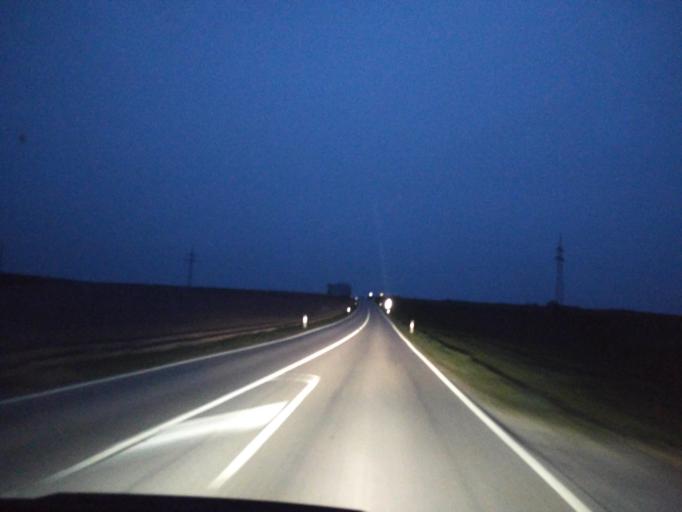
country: DE
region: Bavaria
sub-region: Upper Bavaria
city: Griesstatt
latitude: 47.9878
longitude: 12.1838
